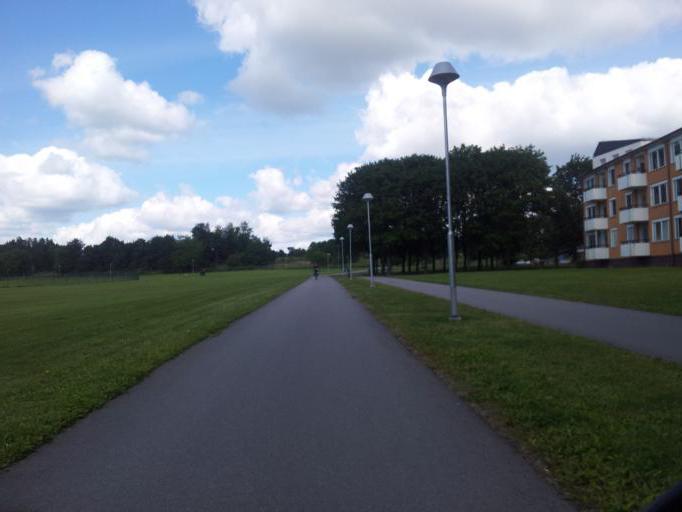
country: SE
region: Uppsala
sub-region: Uppsala Kommun
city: Uppsala
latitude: 59.8742
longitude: 17.6645
